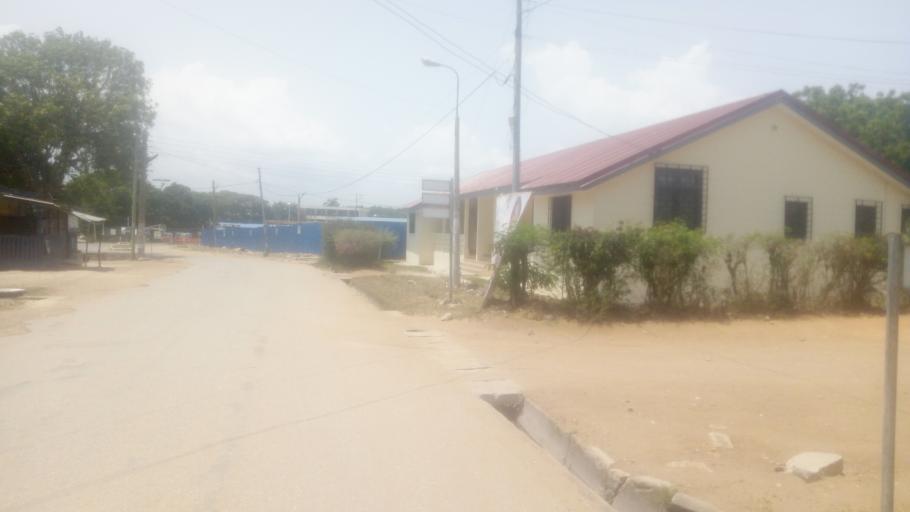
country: GH
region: Central
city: Winneba
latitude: 5.3623
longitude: -0.6314
